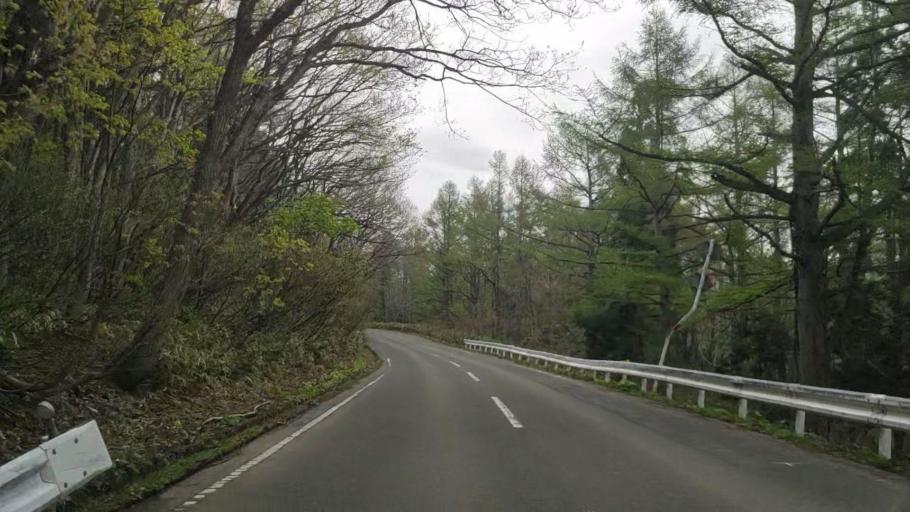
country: JP
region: Aomori
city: Aomori Shi
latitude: 40.7321
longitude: 140.8408
